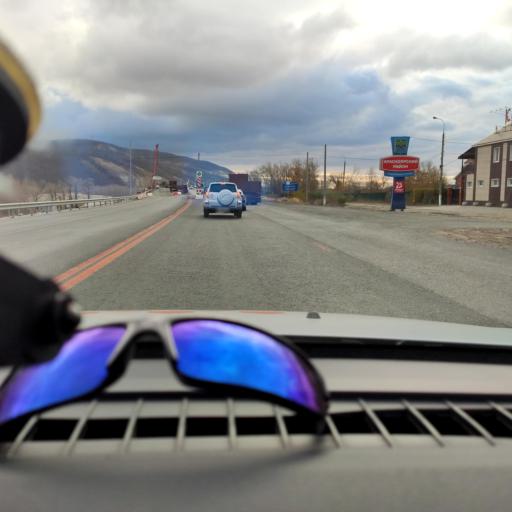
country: RU
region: Samara
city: Volzhskiy
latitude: 53.4160
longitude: 50.1308
